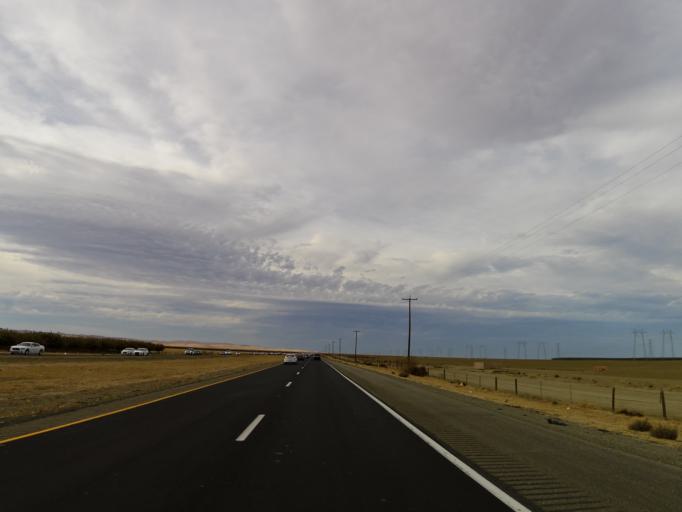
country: US
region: California
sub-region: Kings County
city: Kettleman City
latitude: 35.8895
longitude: -119.8657
